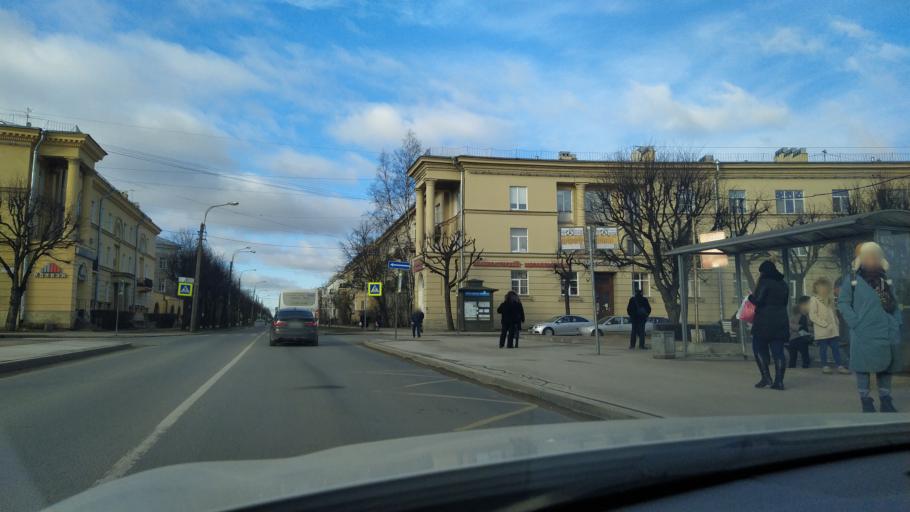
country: RU
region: St.-Petersburg
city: Pushkin
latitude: 59.7233
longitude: 30.4278
